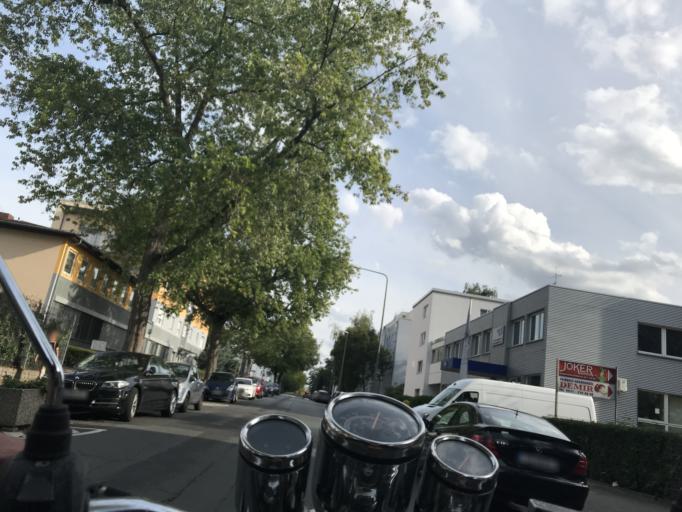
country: DE
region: Hesse
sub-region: Regierungsbezirk Darmstadt
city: Wiesbaden
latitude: 50.0644
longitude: 8.2566
